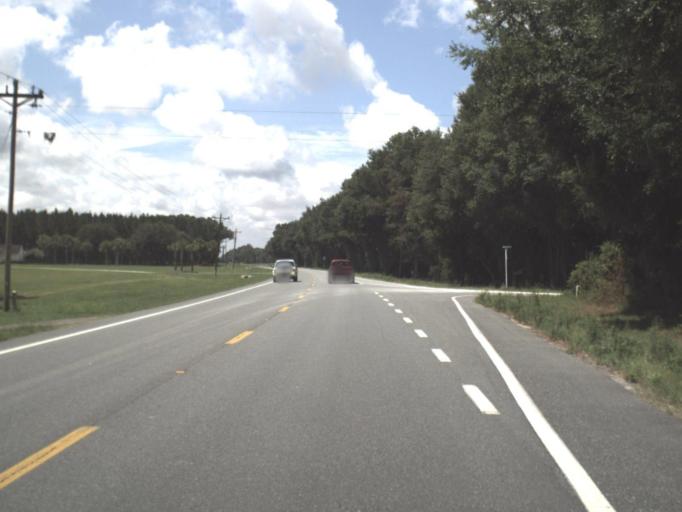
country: US
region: Florida
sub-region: Gilchrist County
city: Trenton
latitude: 29.8369
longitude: -82.8672
